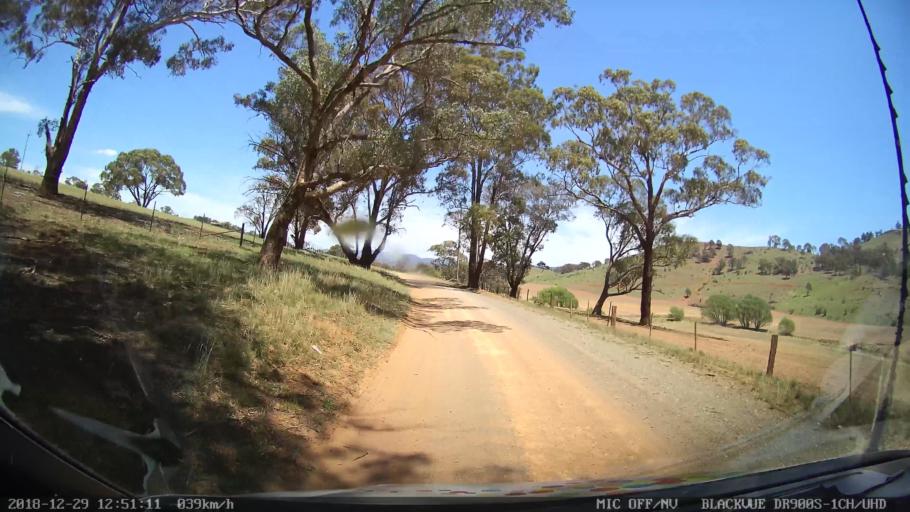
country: AU
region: Australian Capital Territory
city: Macarthur
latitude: -35.6736
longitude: 149.1998
